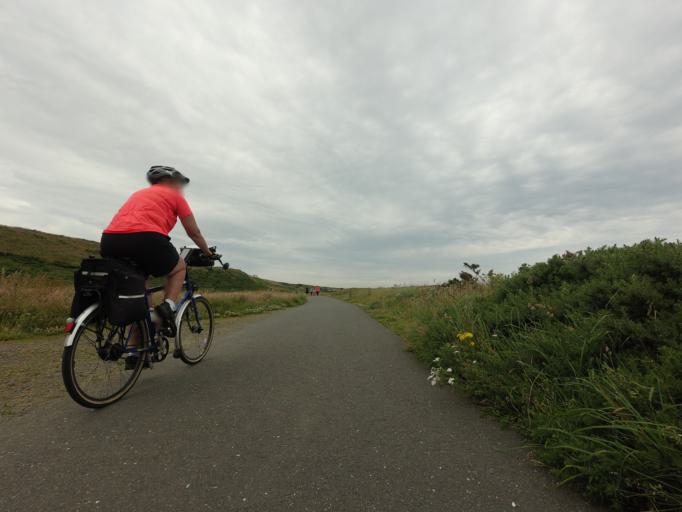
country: GB
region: Scotland
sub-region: Aberdeenshire
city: Whitehills
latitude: 57.6724
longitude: -2.5606
